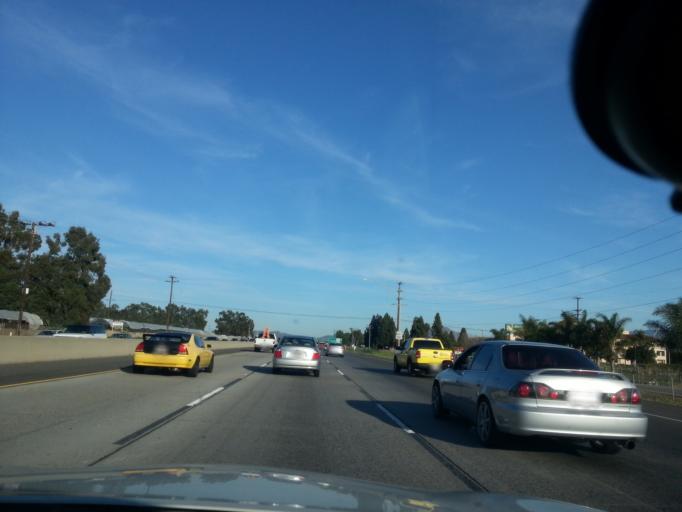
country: US
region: California
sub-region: Ventura County
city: Camarillo
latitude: 34.2213
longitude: -119.0977
